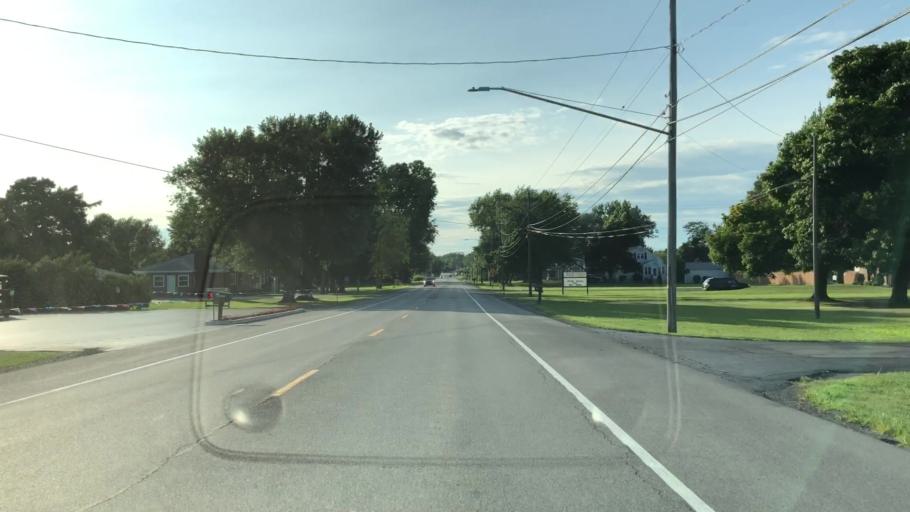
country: US
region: New York
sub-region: Erie County
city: West Seneca
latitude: 42.8623
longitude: -78.7677
